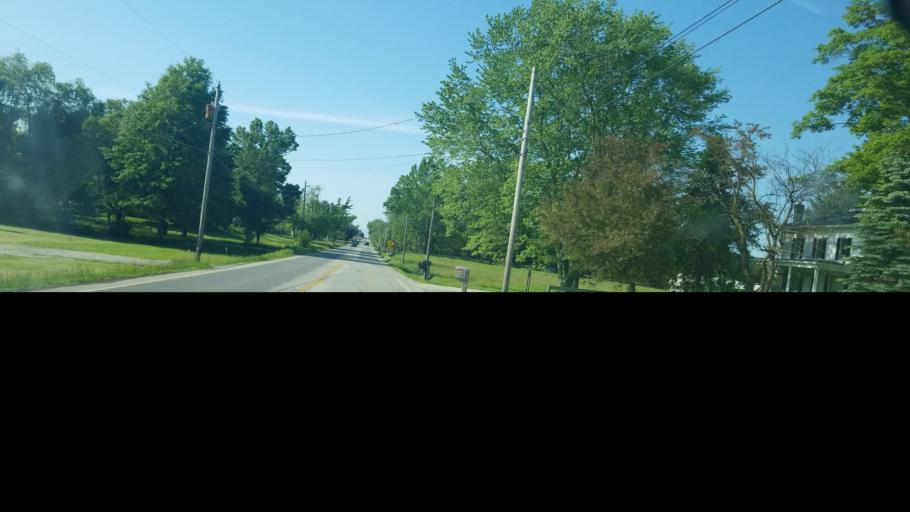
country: US
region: Ohio
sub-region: Medina County
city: Seville
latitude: 41.0701
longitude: -81.8643
